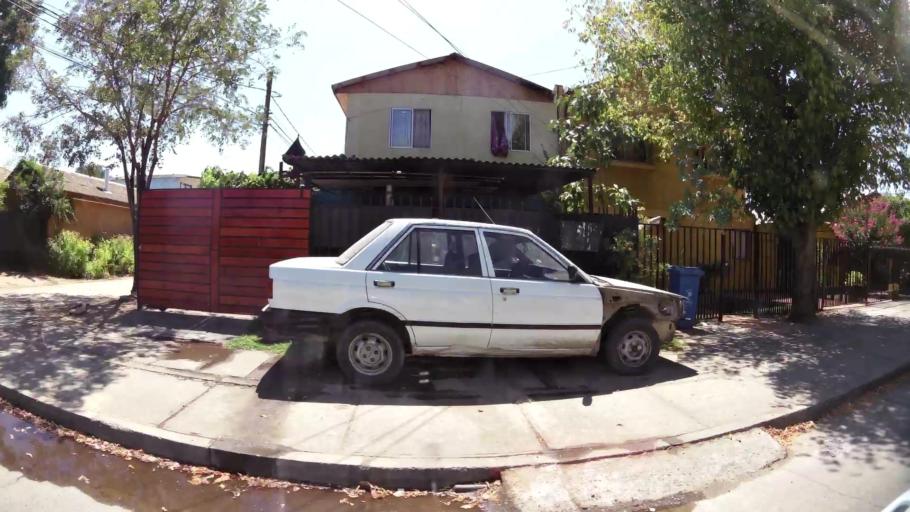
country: CL
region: Maule
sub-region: Provincia de Talca
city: Talca
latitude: -35.4318
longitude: -71.6334
